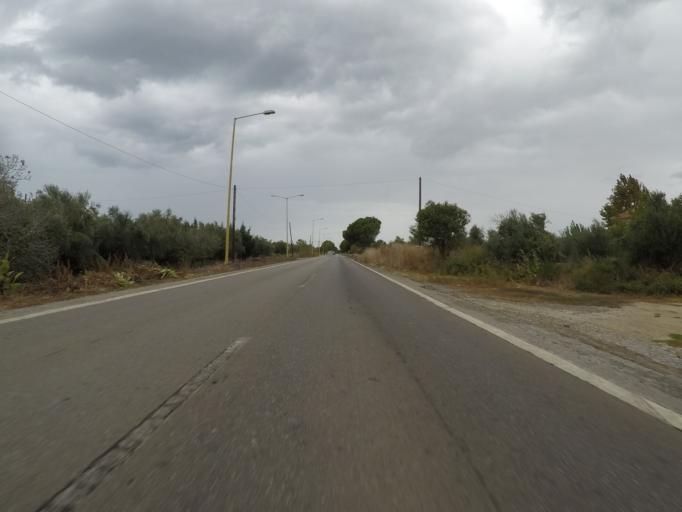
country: GR
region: West Greece
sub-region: Nomos Ileias
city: Zacharo
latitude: 37.4891
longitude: 21.6251
